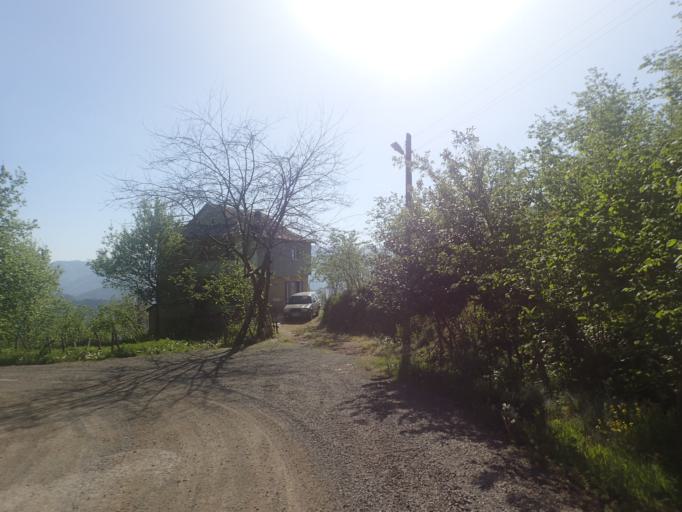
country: TR
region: Ordu
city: Kabaduz
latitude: 40.7957
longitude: 37.9049
